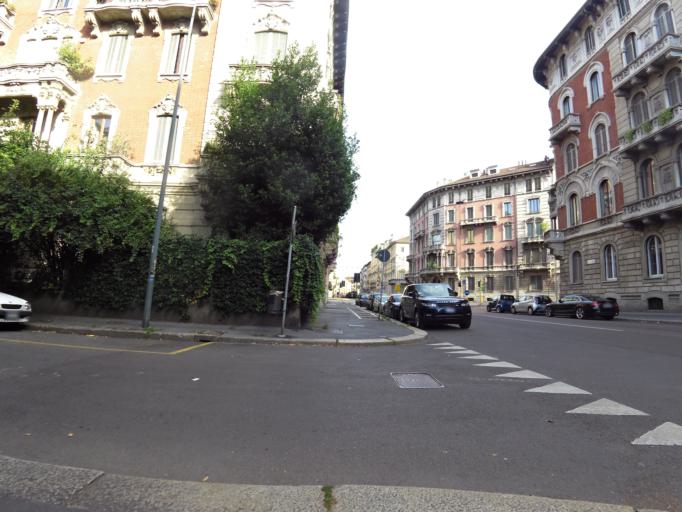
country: IT
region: Lombardy
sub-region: Citta metropolitana di Milano
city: Milano
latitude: 45.4680
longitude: 9.1681
